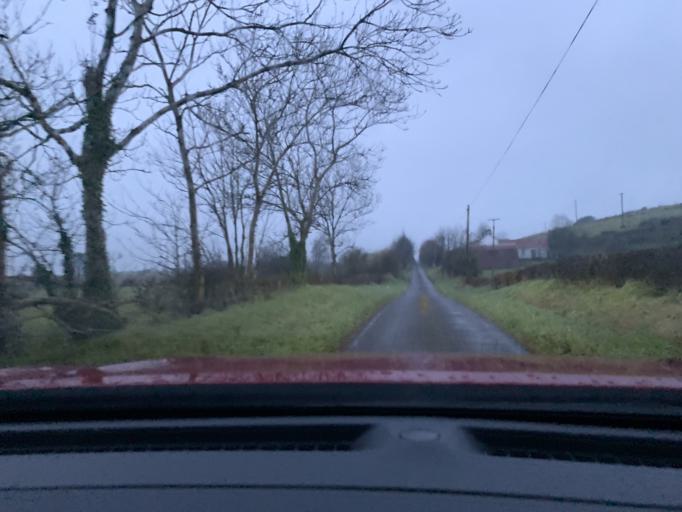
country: IE
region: Connaught
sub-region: Sligo
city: Ballymote
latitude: 54.0193
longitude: -8.5380
